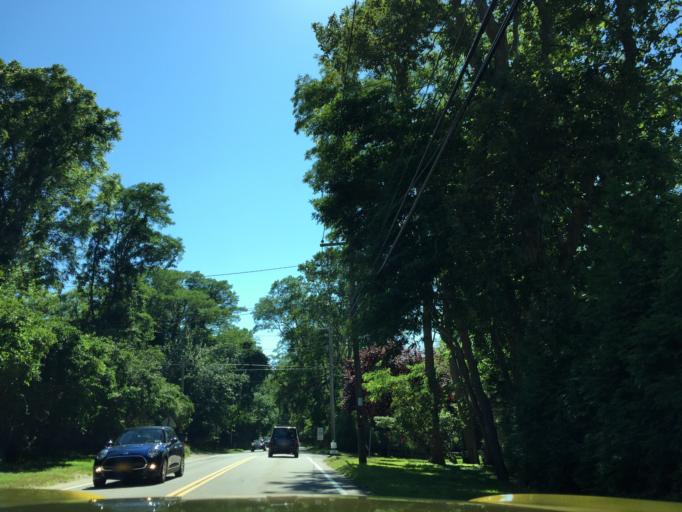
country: US
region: New York
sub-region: Suffolk County
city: Noyack
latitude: 40.9887
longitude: -72.3631
